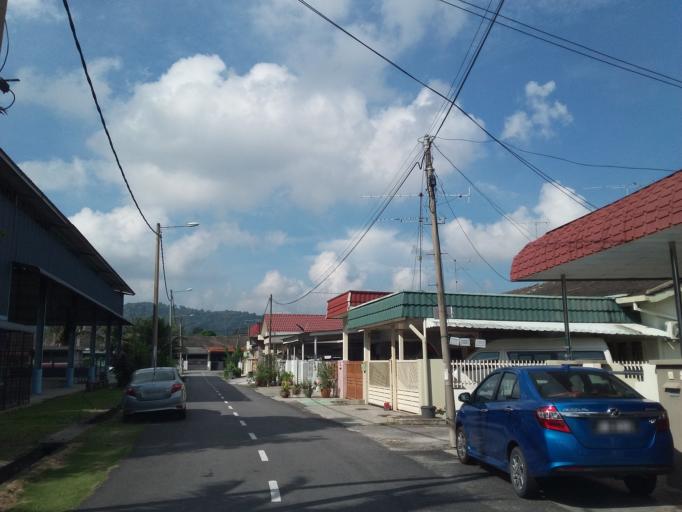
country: MY
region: Johor
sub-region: Daerah Batu Pahat
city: Batu Pahat
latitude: 1.8407
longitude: 102.9264
